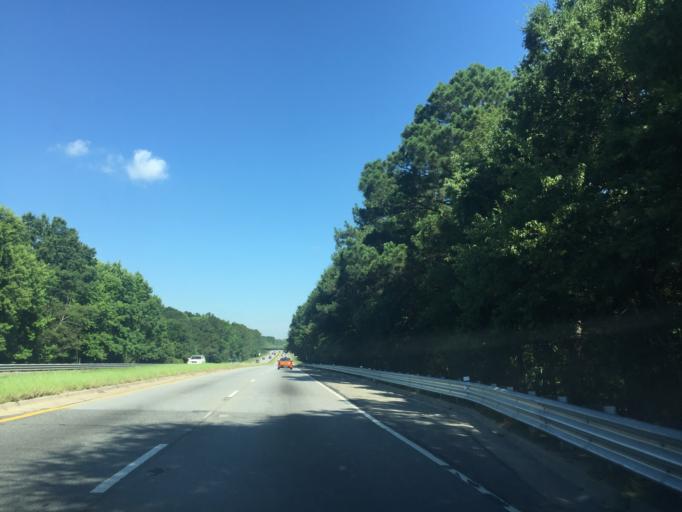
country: US
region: Georgia
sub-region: Chatham County
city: Savannah
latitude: 32.0356
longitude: -81.1349
